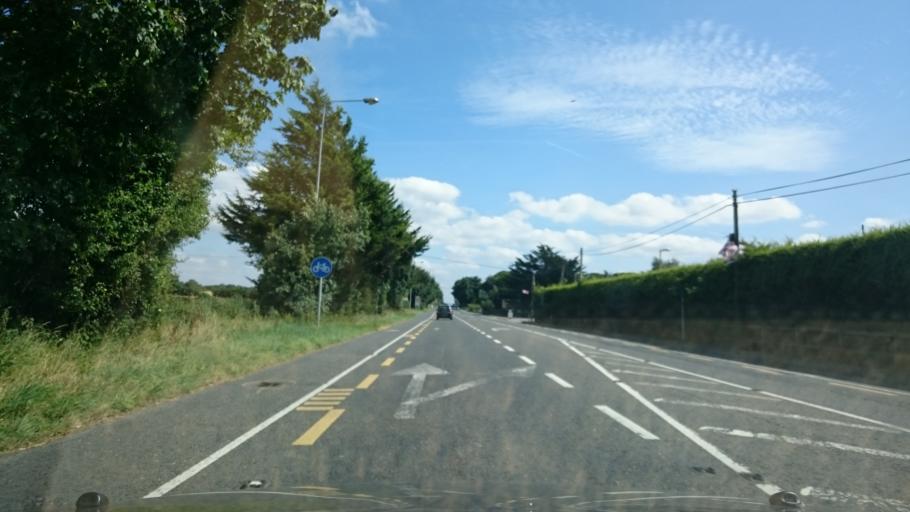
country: IE
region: Leinster
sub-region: Kilkenny
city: Kilkenny
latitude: 52.6465
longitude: -7.1463
